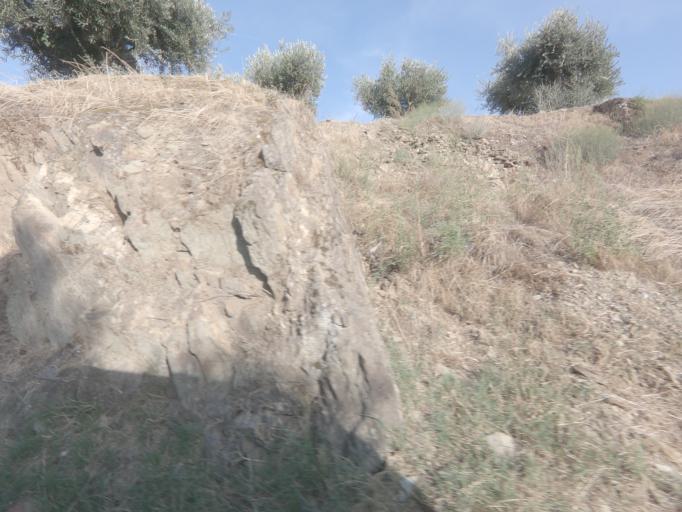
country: PT
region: Vila Real
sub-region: Sabrosa
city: Sabrosa
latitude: 41.2173
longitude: -7.5405
